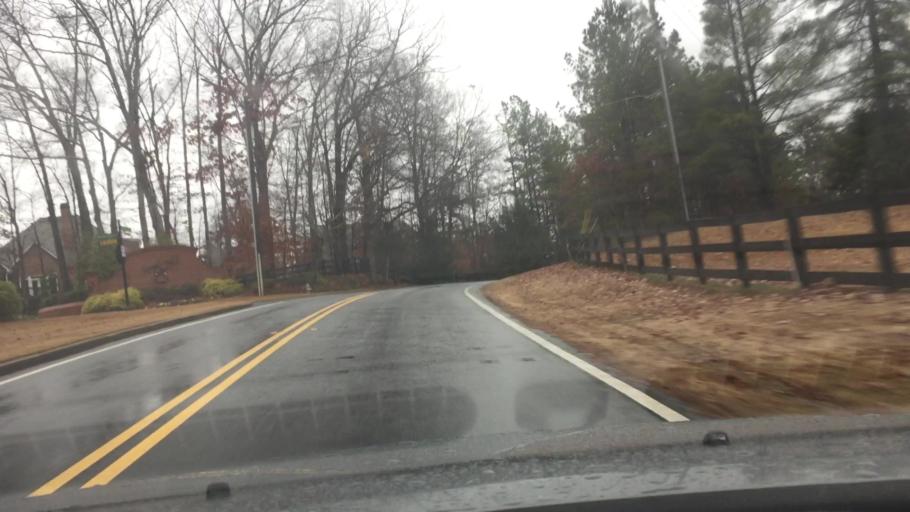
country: US
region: Georgia
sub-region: Cobb County
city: Kennesaw
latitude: 33.9717
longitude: -84.6346
